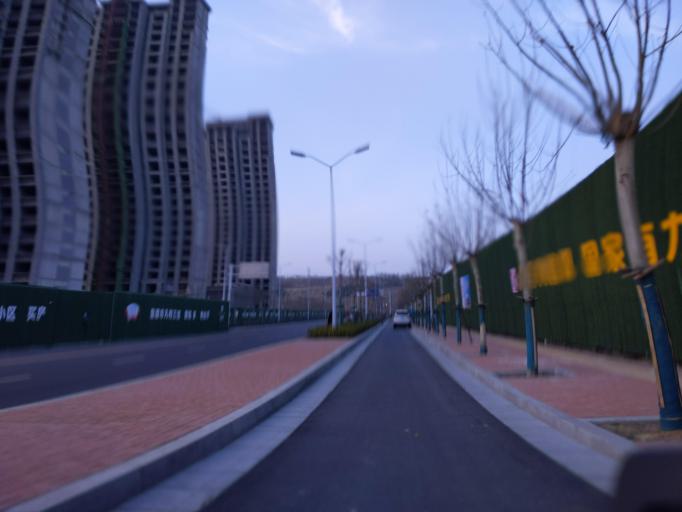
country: CN
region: Henan Sheng
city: Puyang
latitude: 35.8150
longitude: 115.0119
